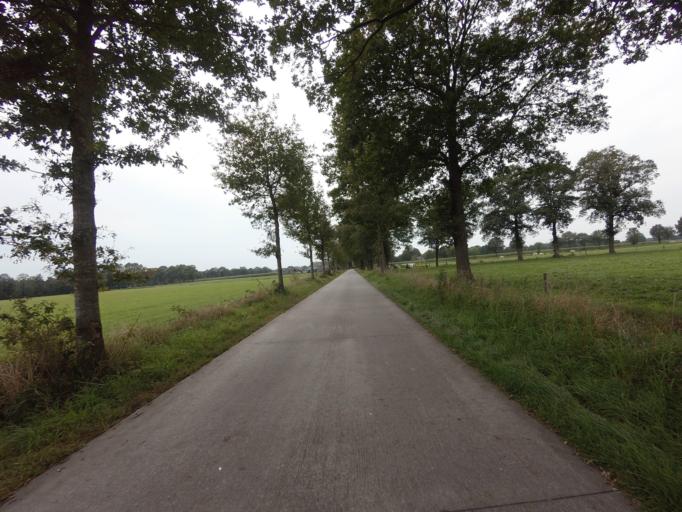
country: NL
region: Gelderland
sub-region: Gemeente Lochem
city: Harfsen
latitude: 52.2809
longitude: 6.3261
